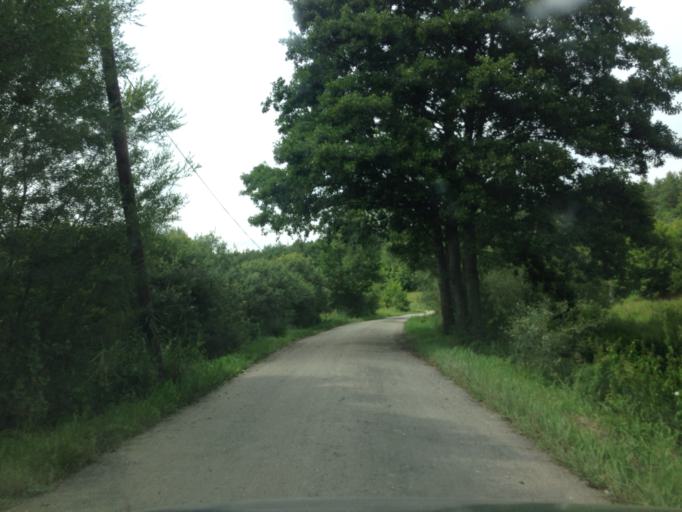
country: PL
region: Kujawsko-Pomorskie
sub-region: Powiat brodnicki
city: Brodnica
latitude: 53.2806
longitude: 19.4764
